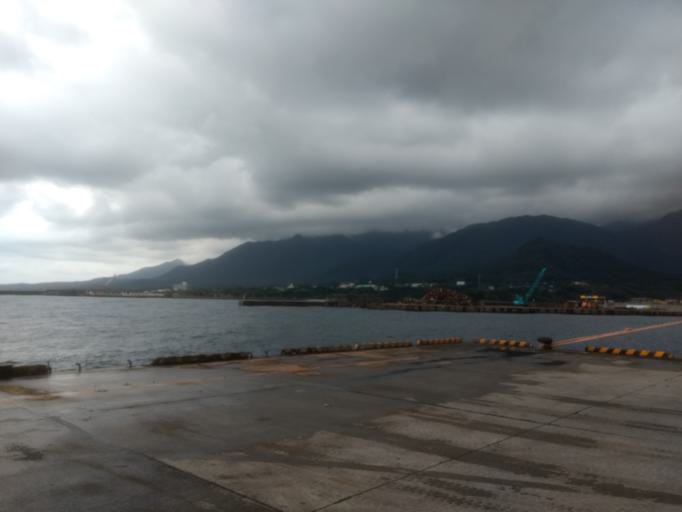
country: JP
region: Kagoshima
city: Nishinoomote
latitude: 30.4319
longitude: 130.5741
